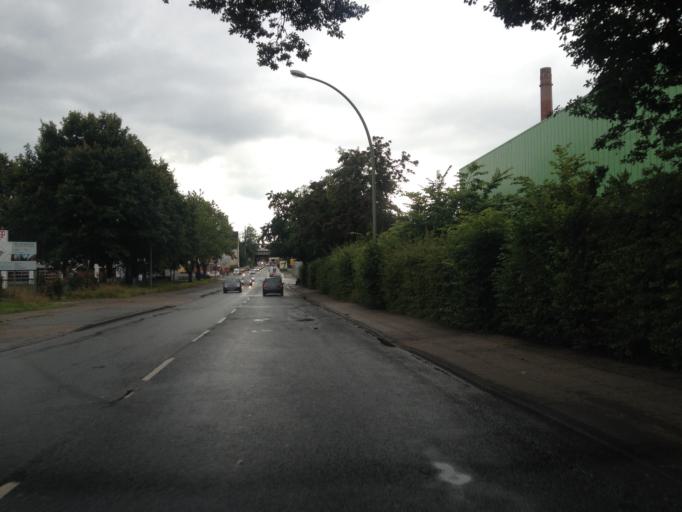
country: DE
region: North Rhine-Westphalia
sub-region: Regierungsbezirk Detmold
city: Bielefeld
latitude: 52.0376
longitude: 8.5435
